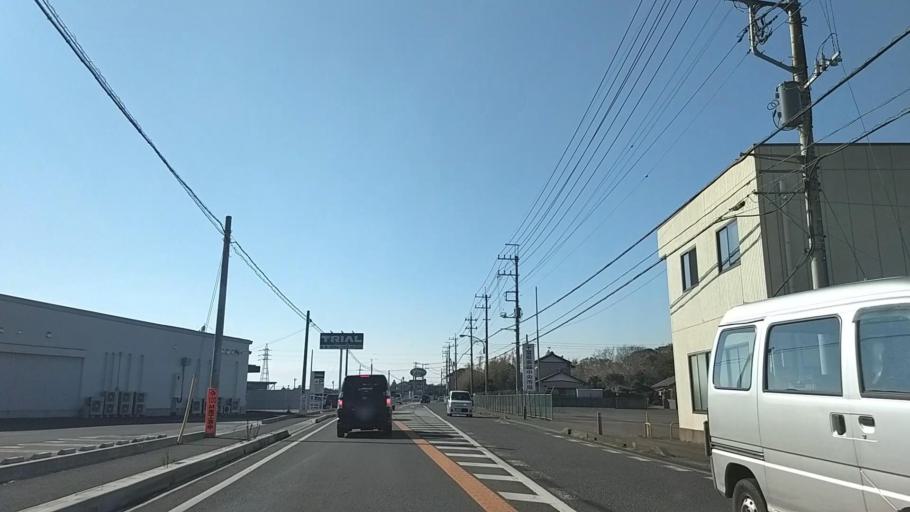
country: JP
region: Chiba
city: Yokaichiba
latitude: 35.7162
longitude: 140.5850
